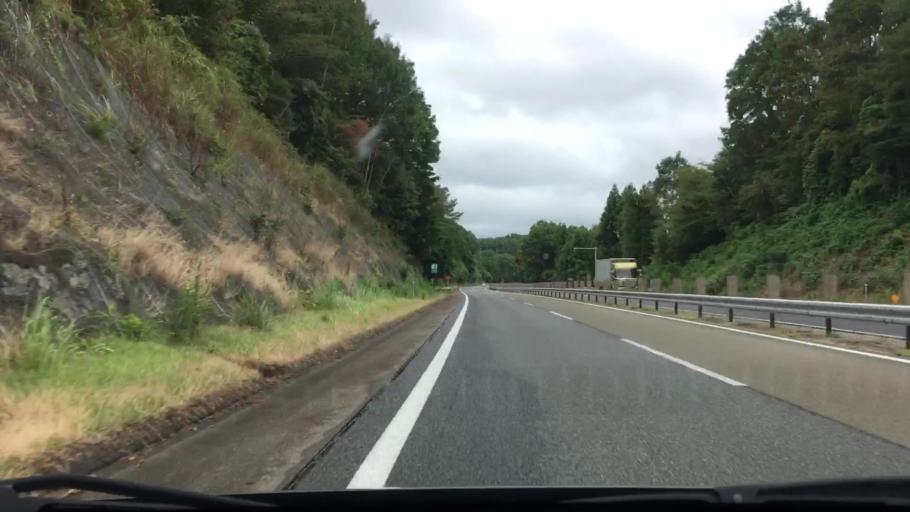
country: JP
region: Hiroshima
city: Miyoshi
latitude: 34.7921
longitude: 132.8829
